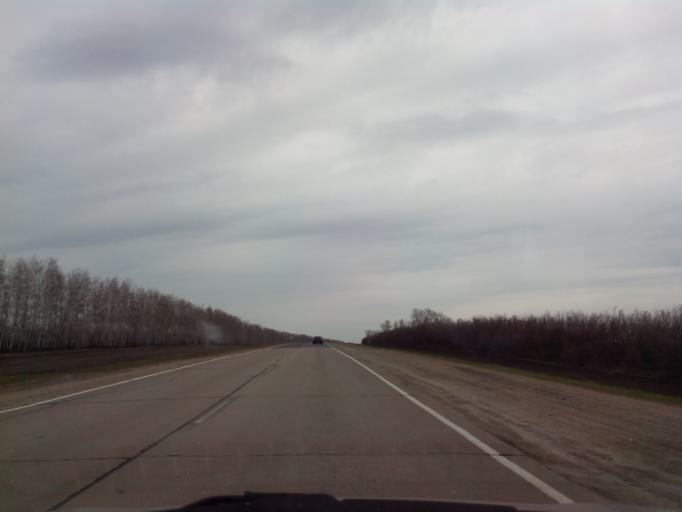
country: RU
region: Tambov
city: Znamenka
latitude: 52.4740
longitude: 41.3642
